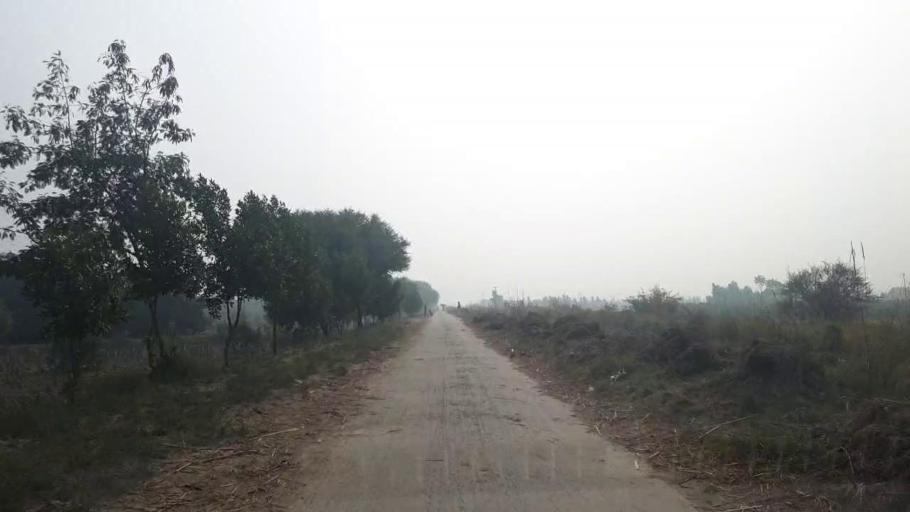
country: PK
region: Sindh
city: Tando Adam
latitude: 25.7657
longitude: 68.6077
